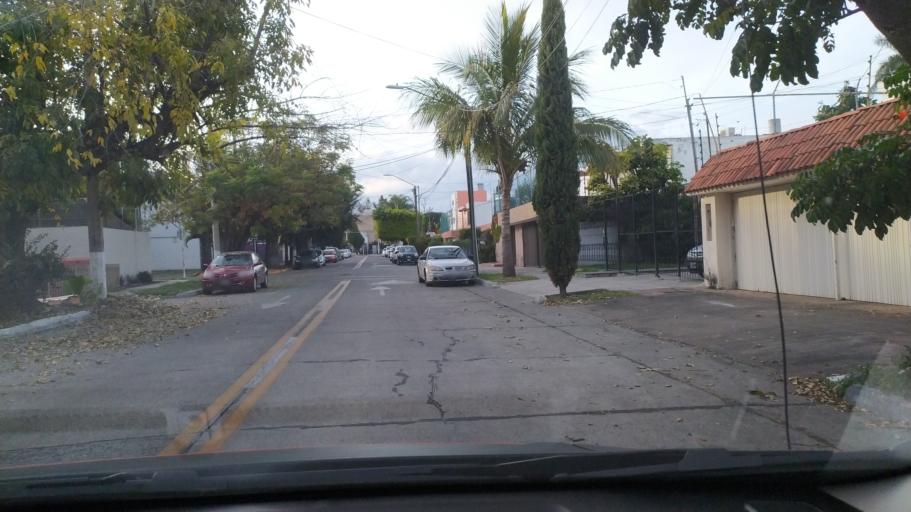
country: MX
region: Jalisco
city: Guadalajara
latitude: 20.6588
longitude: -103.4009
